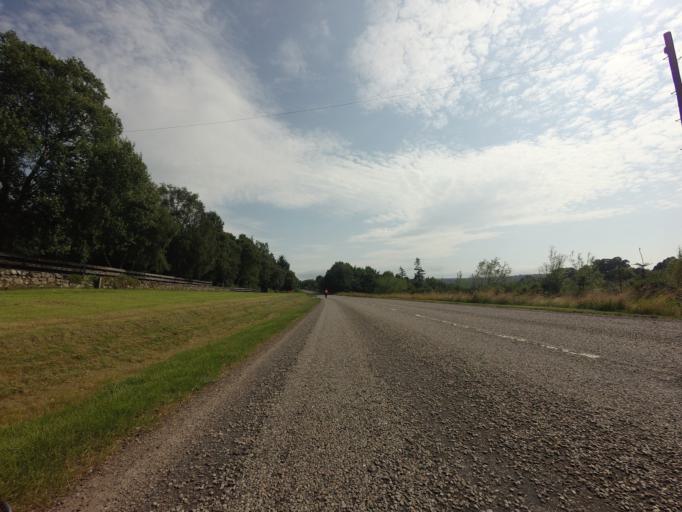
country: GB
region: Scotland
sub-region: Highland
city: Evanton
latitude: 57.9213
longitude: -4.3986
